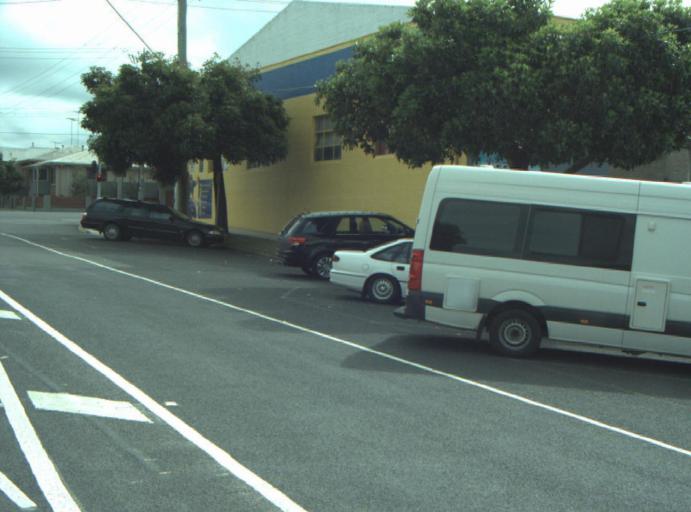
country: AU
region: Victoria
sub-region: Greater Geelong
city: Geelong
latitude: -38.1629
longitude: 144.3564
